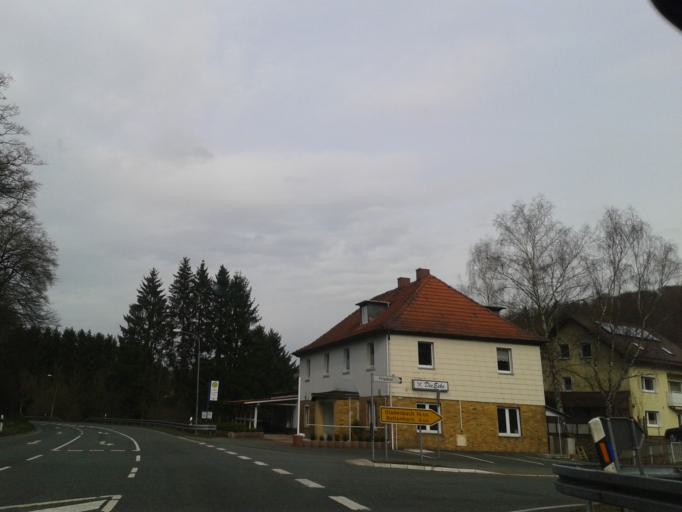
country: DE
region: Hesse
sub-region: Regierungsbezirk Giessen
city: Siegbach
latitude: 50.8067
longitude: 8.4310
